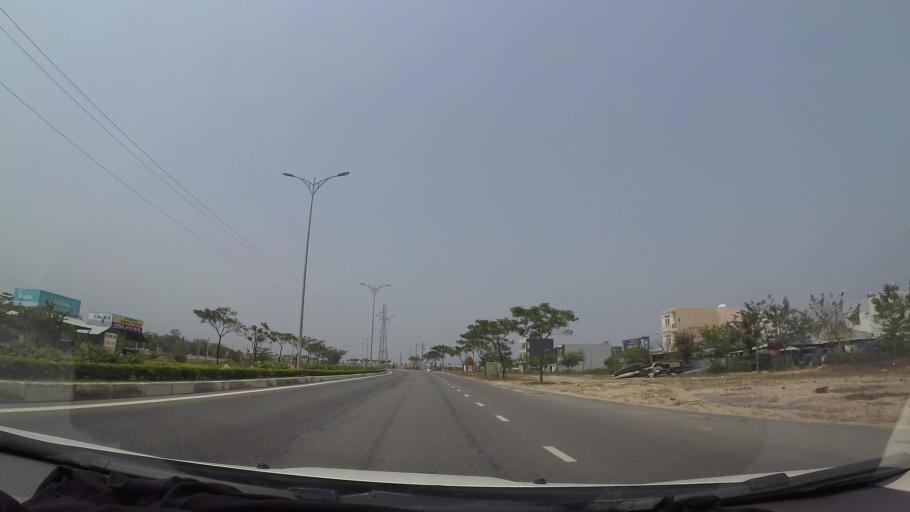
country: VN
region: Da Nang
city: Ngu Hanh Son
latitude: 15.9979
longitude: 108.2340
